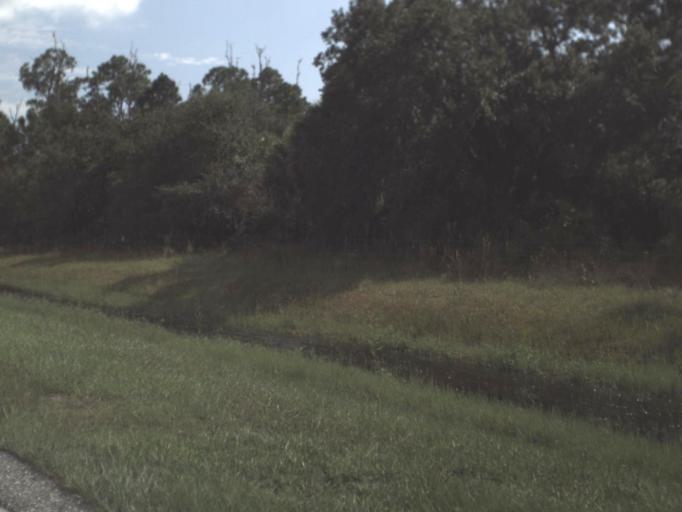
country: US
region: Florida
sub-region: Sarasota County
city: Plantation
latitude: 27.0827
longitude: -82.3329
